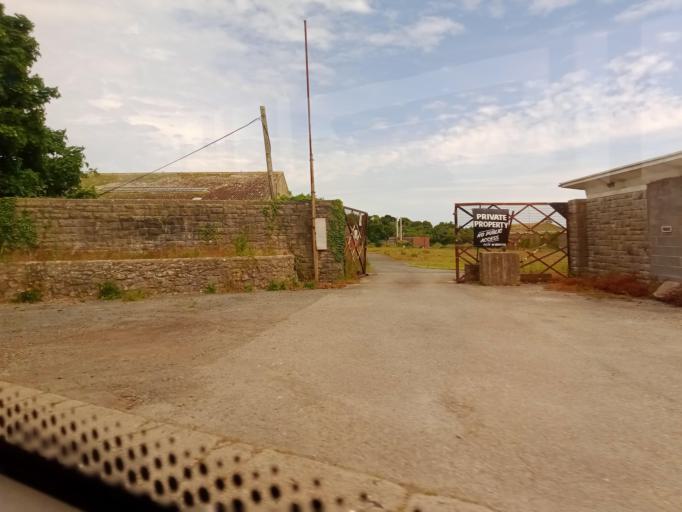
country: GB
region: Wales
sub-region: Anglesey
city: Llangoed
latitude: 53.2755
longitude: -4.0900
